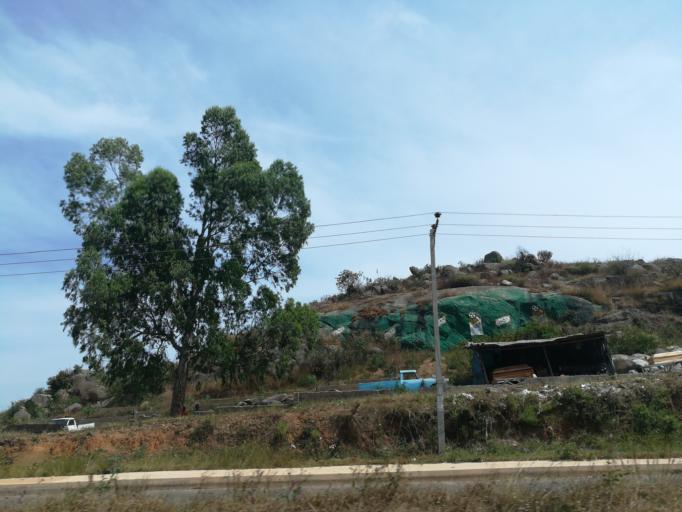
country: NG
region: Plateau
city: Bukuru
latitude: 9.8318
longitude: 8.8671
